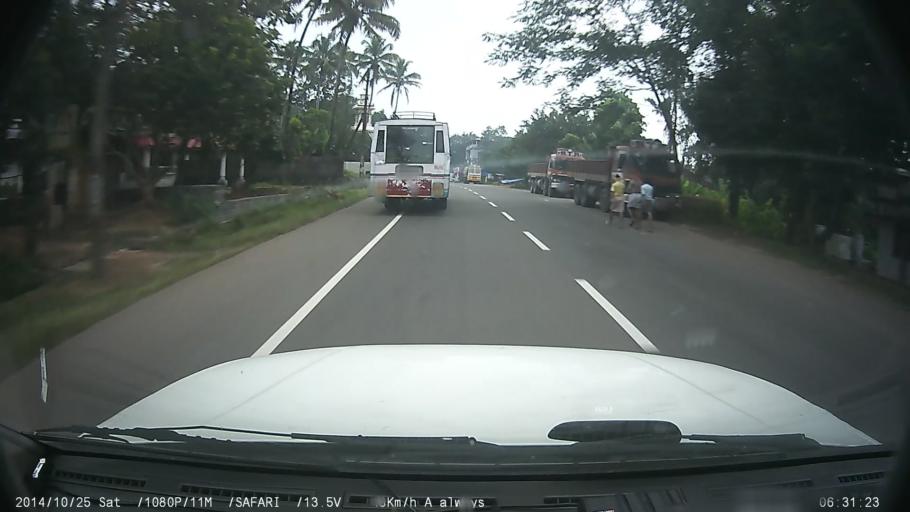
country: IN
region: Kerala
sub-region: Ernakulam
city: Muvattupula
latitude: 10.0273
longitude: 76.5526
